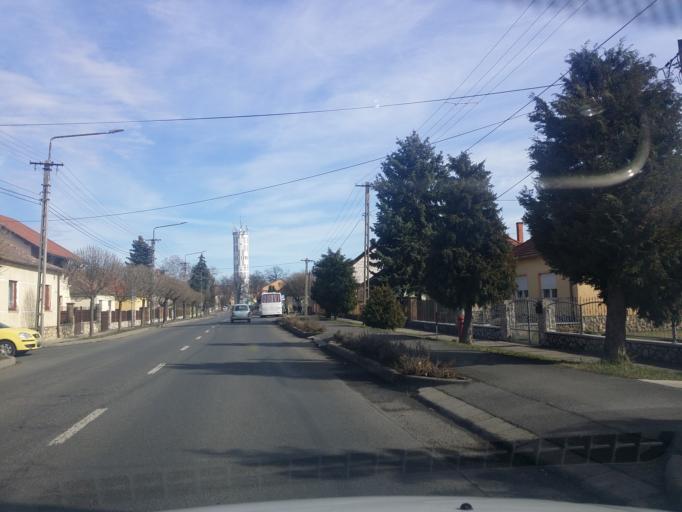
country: HU
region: Baranya
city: Mohacs
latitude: 45.9963
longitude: 18.6756
